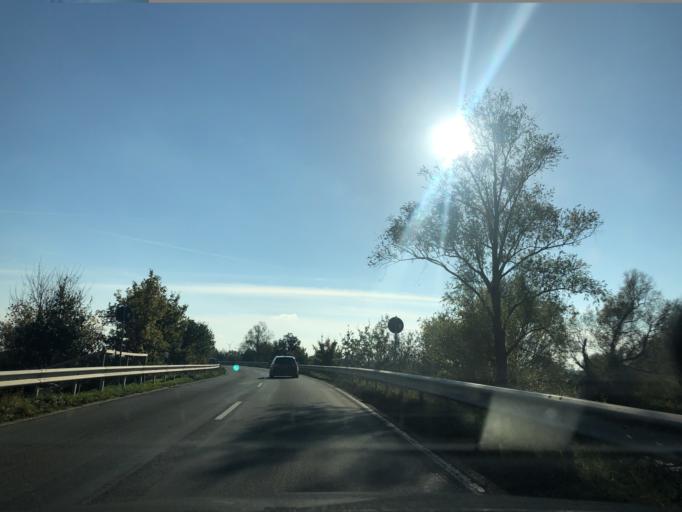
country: DE
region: Lower Saxony
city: Lemwerder
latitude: 53.1747
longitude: 8.5567
